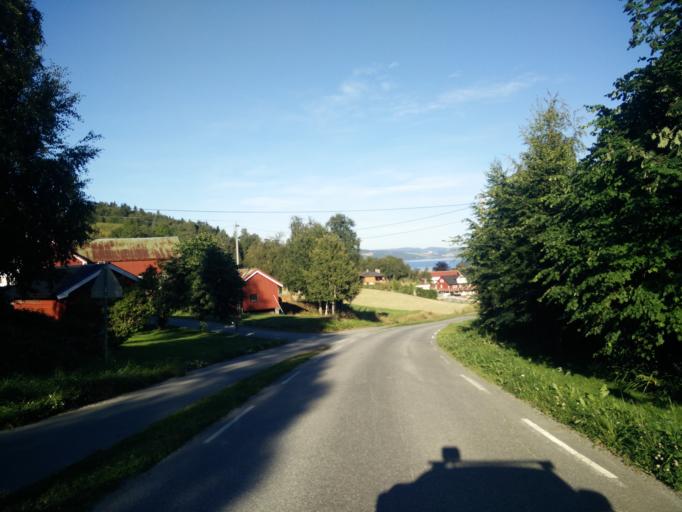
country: NO
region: Sor-Trondelag
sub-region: Skaun
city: Borsa
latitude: 63.3255
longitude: 10.0499
